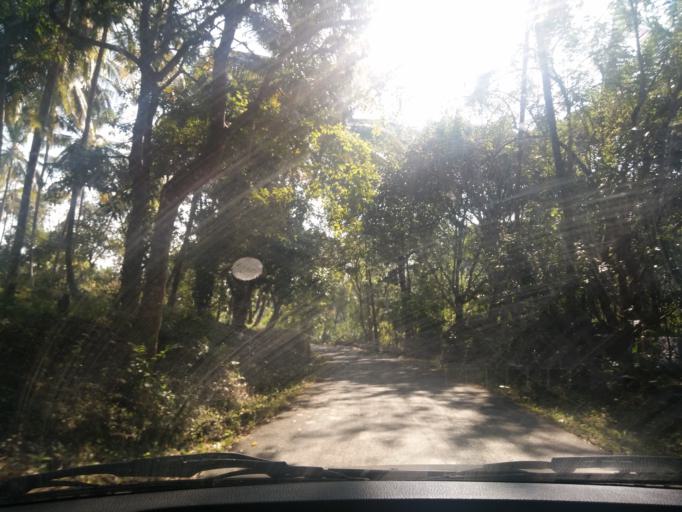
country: IN
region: Goa
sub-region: South Goa
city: Quepem
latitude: 15.1599
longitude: 74.0849
